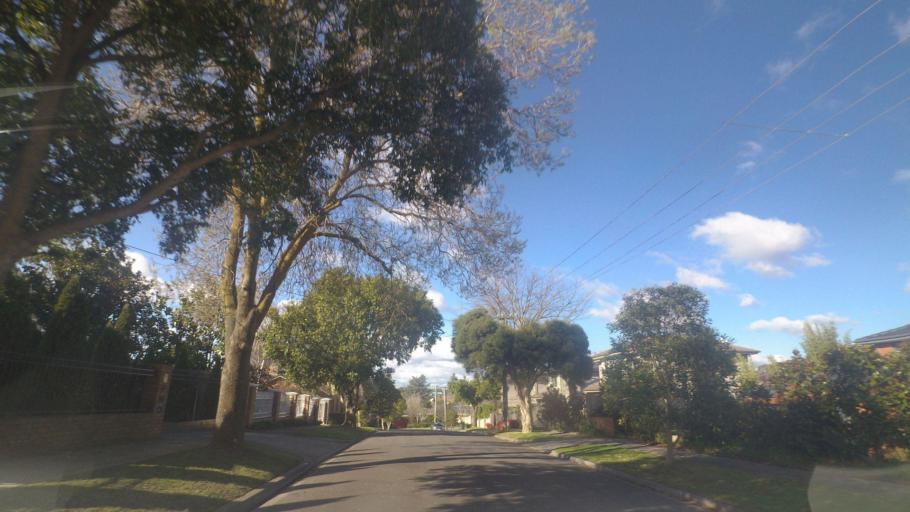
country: AU
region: Victoria
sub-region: Boroondara
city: Balwyn North
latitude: -37.7841
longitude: 145.0891
